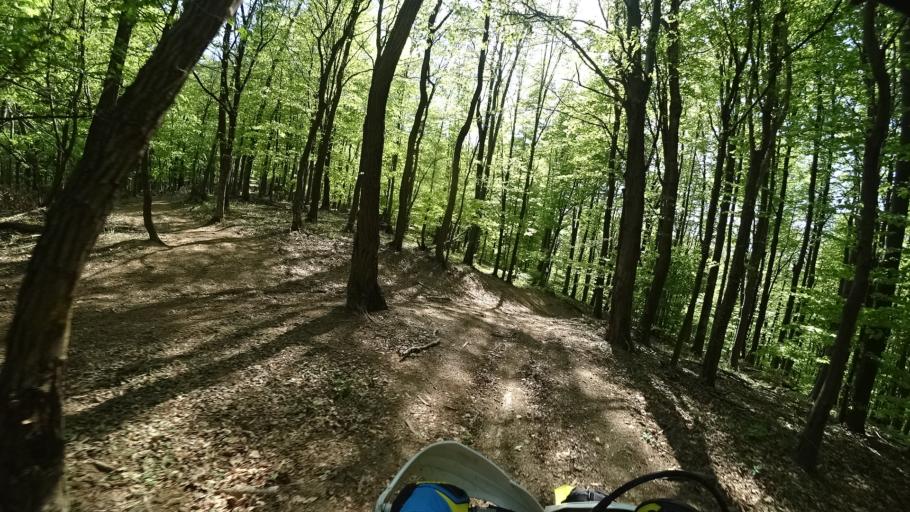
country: HR
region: Zagrebacka
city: Jablanovec
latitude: 45.8832
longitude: 15.9014
